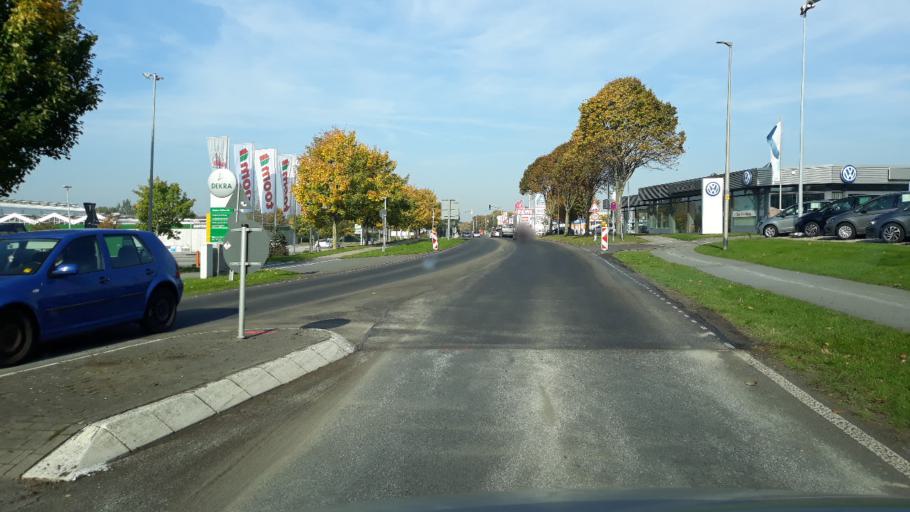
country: DE
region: Schleswig-Holstein
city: Schleswig
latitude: 54.5308
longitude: 9.5737
